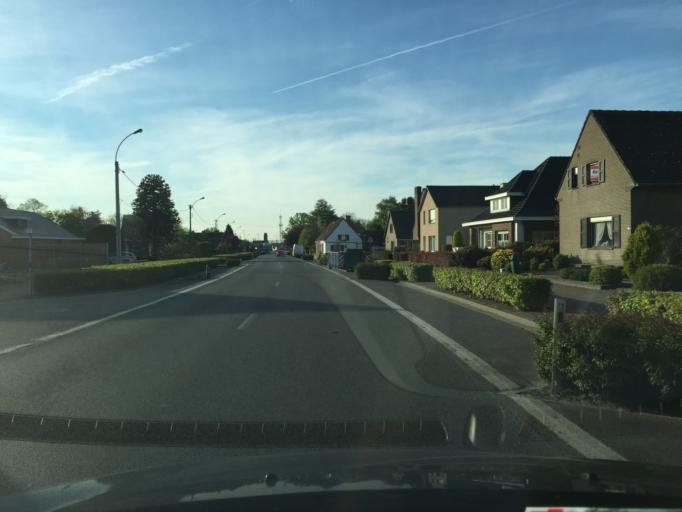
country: BE
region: Flanders
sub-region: Provincie Oost-Vlaanderen
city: Aalter
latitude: 51.1006
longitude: 3.4401
